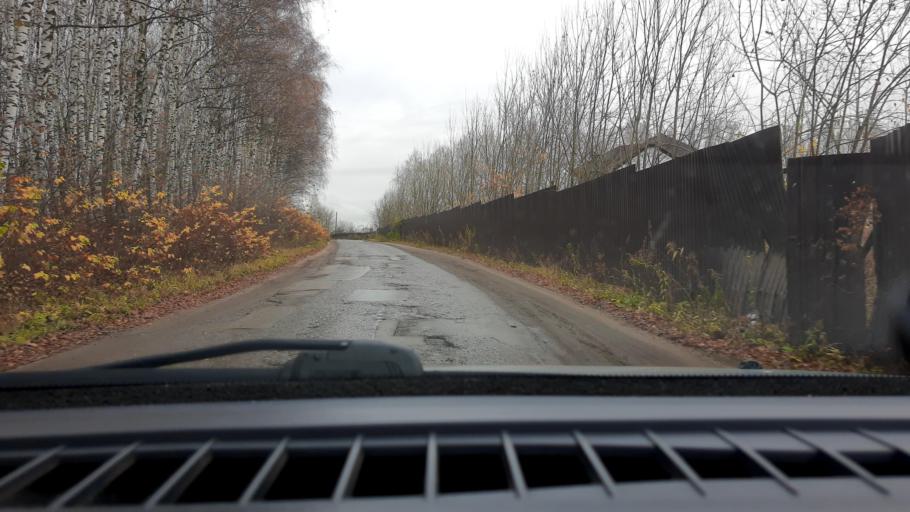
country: RU
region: Nizjnij Novgorod
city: Afonino
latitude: 56.1916
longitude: 44.1074
